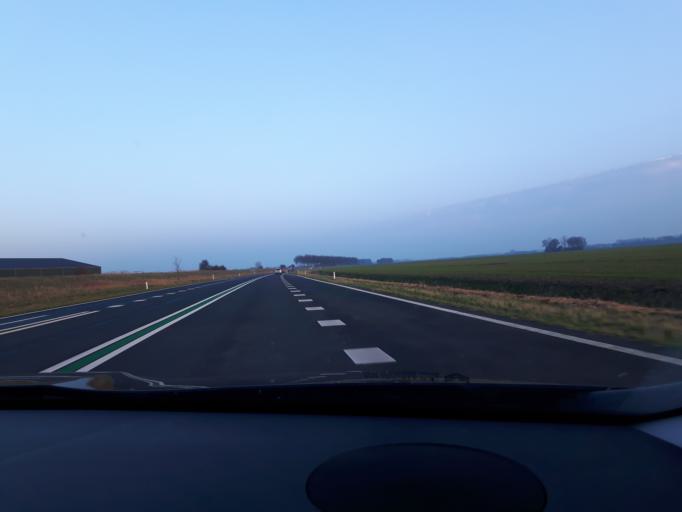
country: NL
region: Zeeland
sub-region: Gemeente Goes
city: Goes
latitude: 51.5780
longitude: 3.8134
